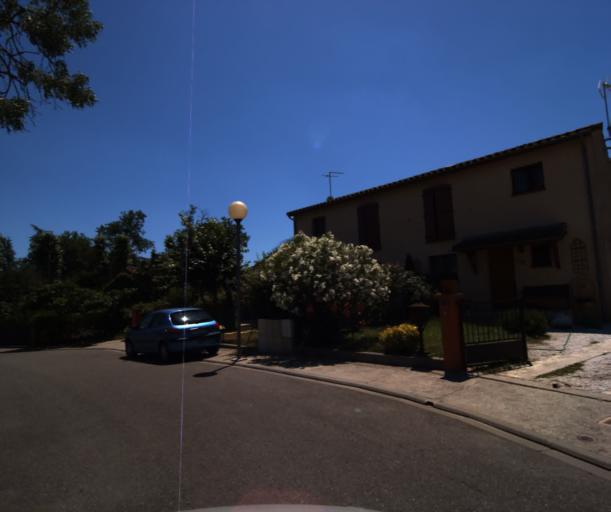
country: FR
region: Midi-Pyrenees
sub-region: Departement de la Haute-Garonne
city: Muret
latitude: 43.4620
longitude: 1.3177
